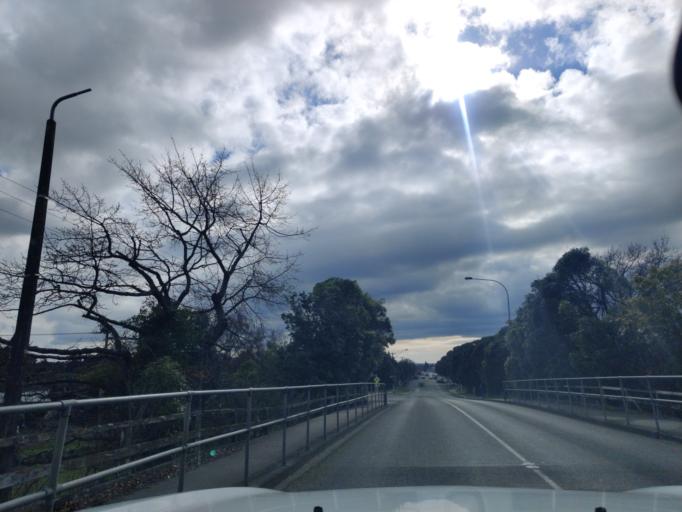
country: NZ
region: Manawatu-Wanganui
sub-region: Palmerston North City
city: Palmerston North
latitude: -40.2961
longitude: 175.7530
